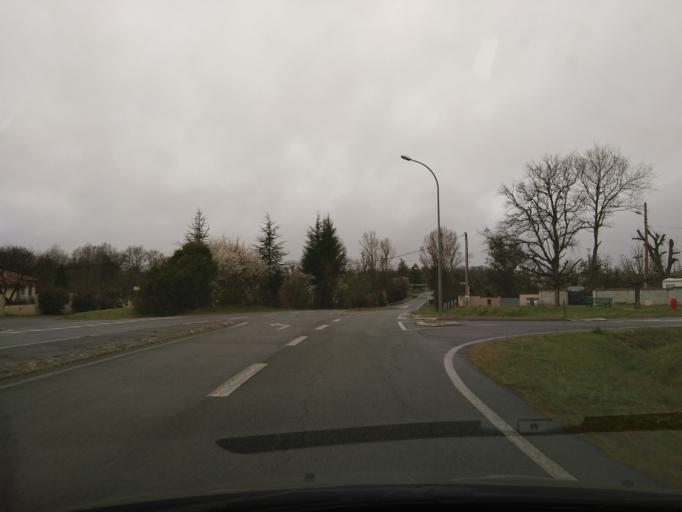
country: FR
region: Midi-Pyrenees
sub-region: Departement de la Haute-Garonne
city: Rieux-Volvestre
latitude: 43.2544
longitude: 1.1964
